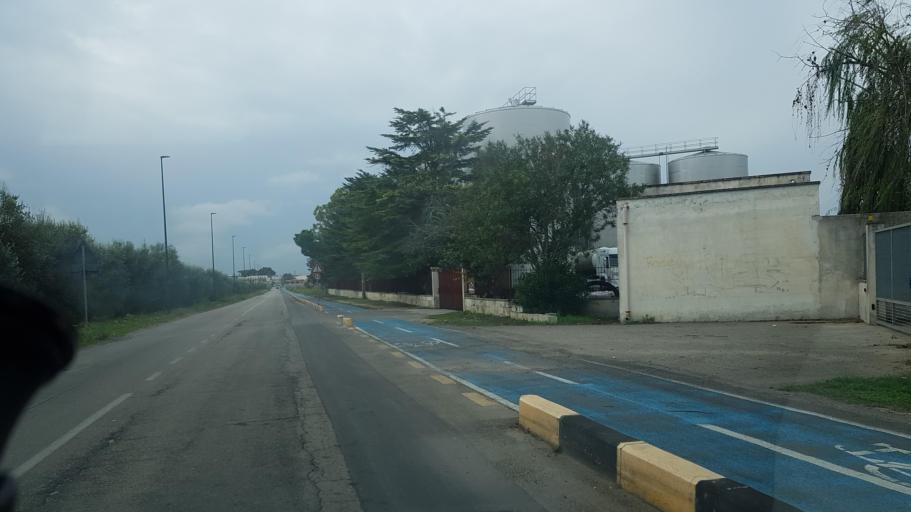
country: IT
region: Apulia
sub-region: Provincia di Lecce
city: Guagnano
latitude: 40.4097
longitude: 17.9566
